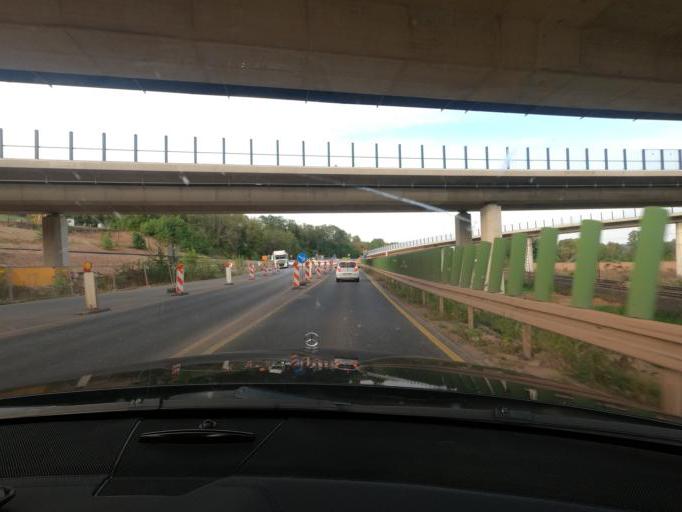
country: DE
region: Hesse
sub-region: Regierungsbezirk Kassel
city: Eschwege
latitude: 51.1461
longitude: 9.9789
